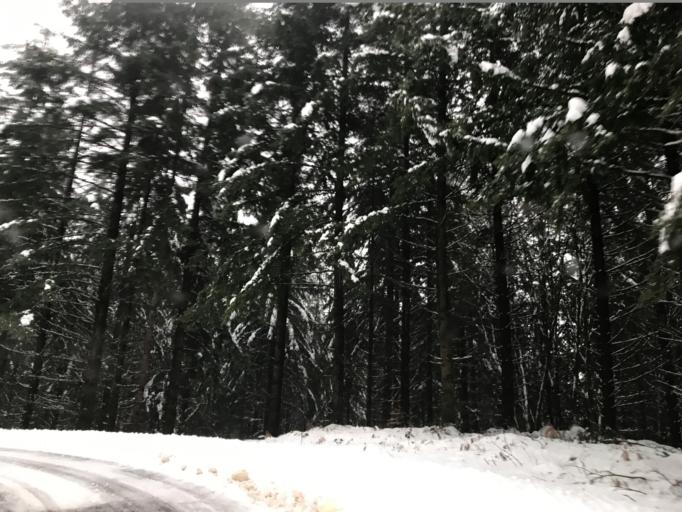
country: FR
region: Auvergne
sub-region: Departement du Puy-de-Dome
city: Celles-sur-Durolle
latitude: 45.7512
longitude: 3.6674
